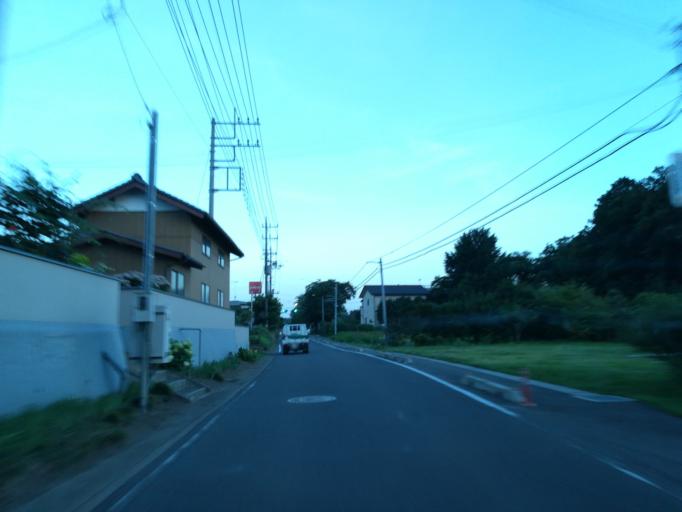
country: JP
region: Ibaraki
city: Makabe
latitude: 36.2955
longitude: 140.0594
